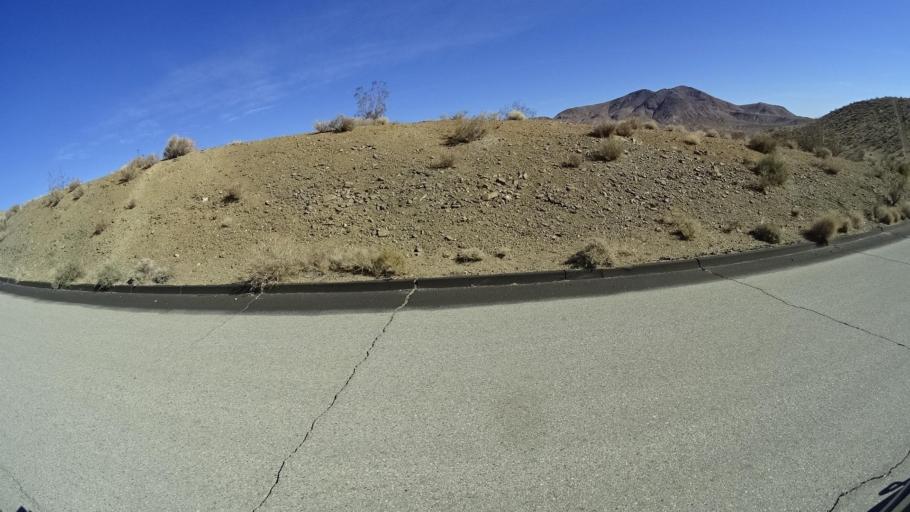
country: US
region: California
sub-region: Kern County
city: Ridgecrest
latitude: 35.3527
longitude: -117.6333
